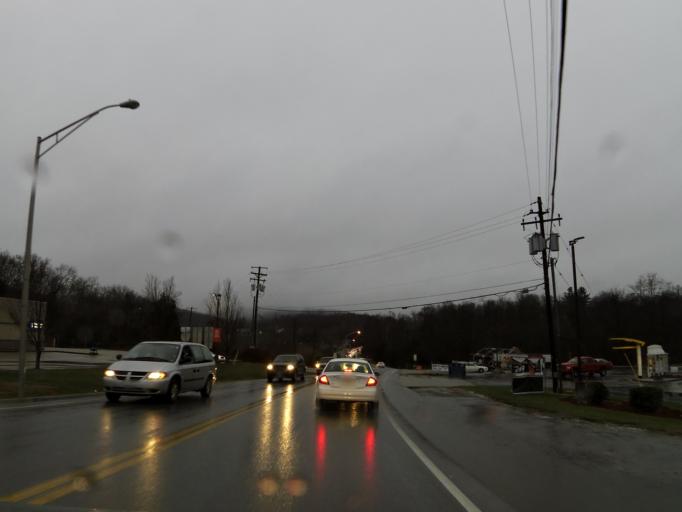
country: US
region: Kentucky
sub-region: Rockcastle County
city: Mount Vernon
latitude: 37.3675
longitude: -84.3367
